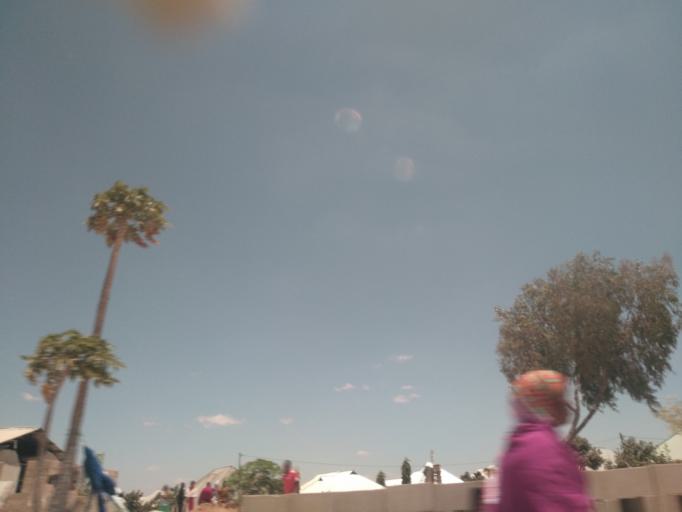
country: TZ
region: Dodoma
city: Dodoma
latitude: -6.1465
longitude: 35.7314
